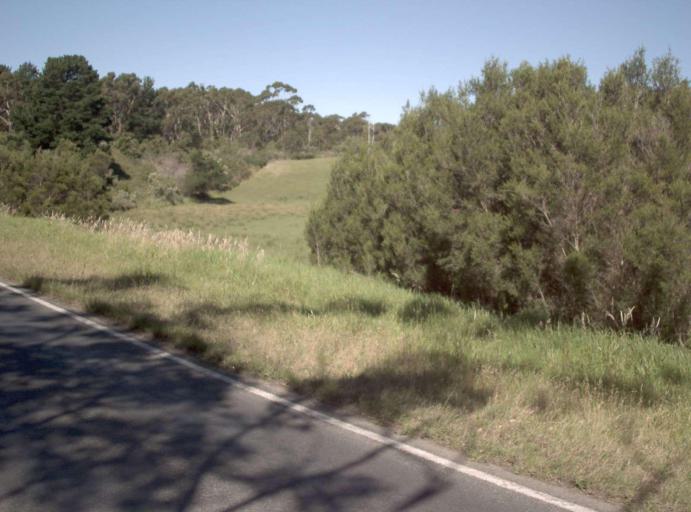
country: AU
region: Victoria
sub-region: Latrobe
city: Morwell
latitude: -38.6702
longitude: 146.3895
